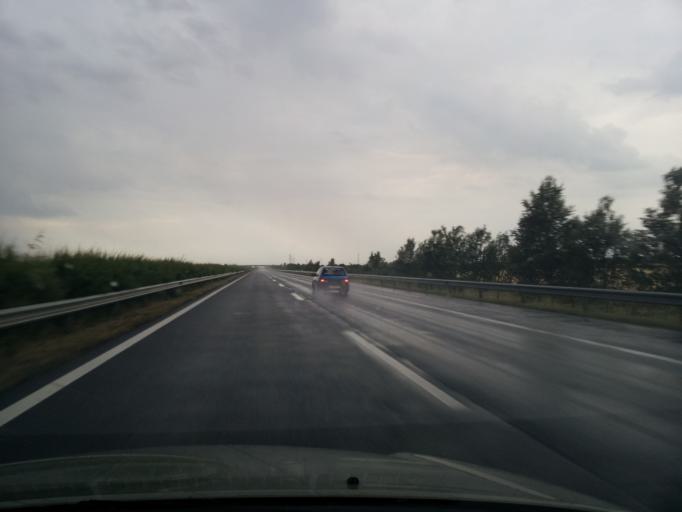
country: HU
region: Borsod-Abauj-Zemplen
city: Onod
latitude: 48.0071
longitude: 20.8819
